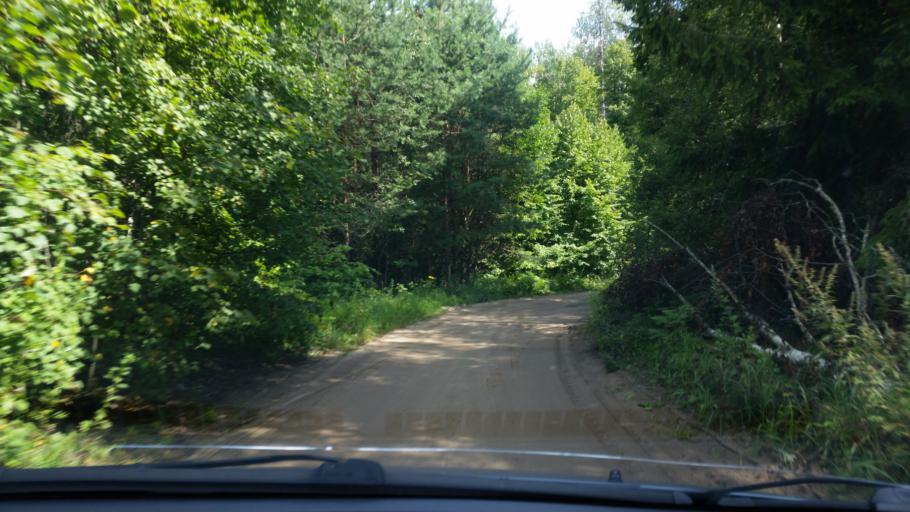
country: RU
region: Moskovskaya
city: Pushchino
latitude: 54.9128
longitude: 37.7179
